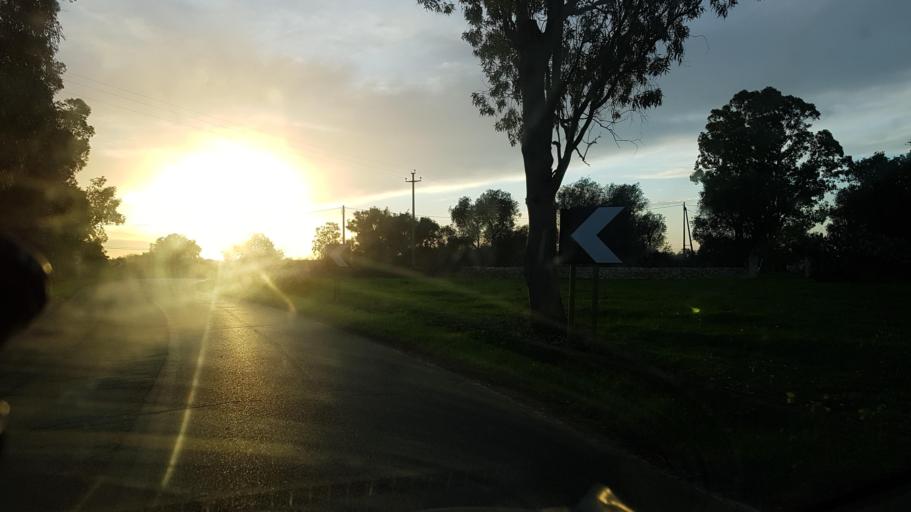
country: IT
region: Apulia
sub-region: Provincia di Brindisi
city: San Michele Salentino
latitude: 40.6424
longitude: 17.5932
